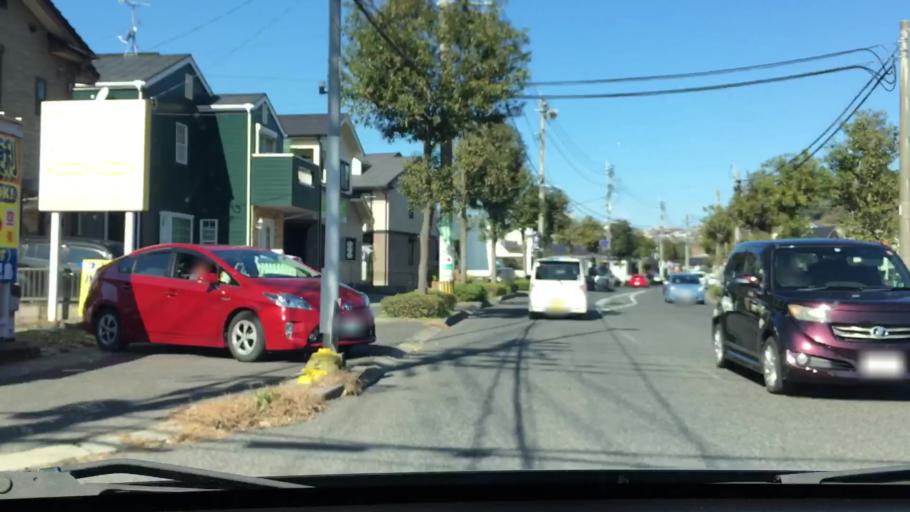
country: JP
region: Kagoshima
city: Kagoshima-shi
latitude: 31.5462
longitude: 130.5338
